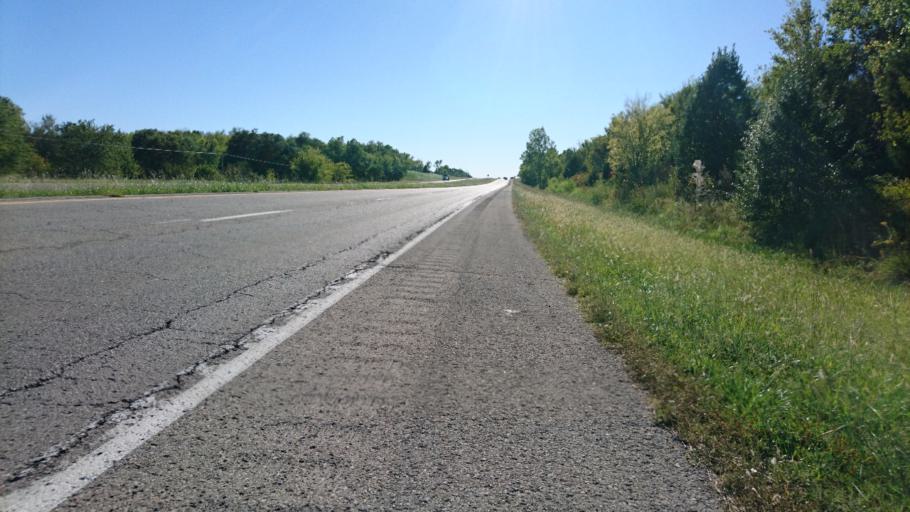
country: US
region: Oklahoma
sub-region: Rogers County
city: Claremore
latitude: 36.3695
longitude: -95.5663
